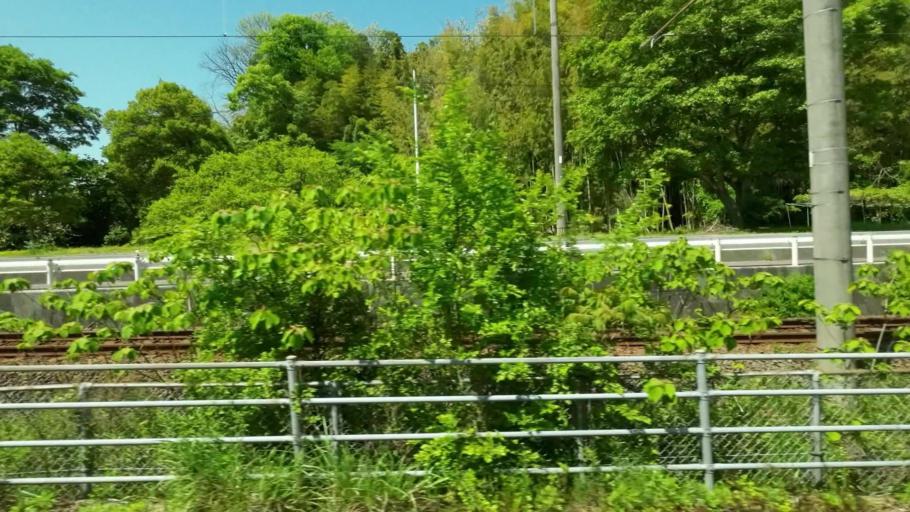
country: JP
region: Ehime
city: Hojo
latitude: 34.0740
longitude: 132.9862
